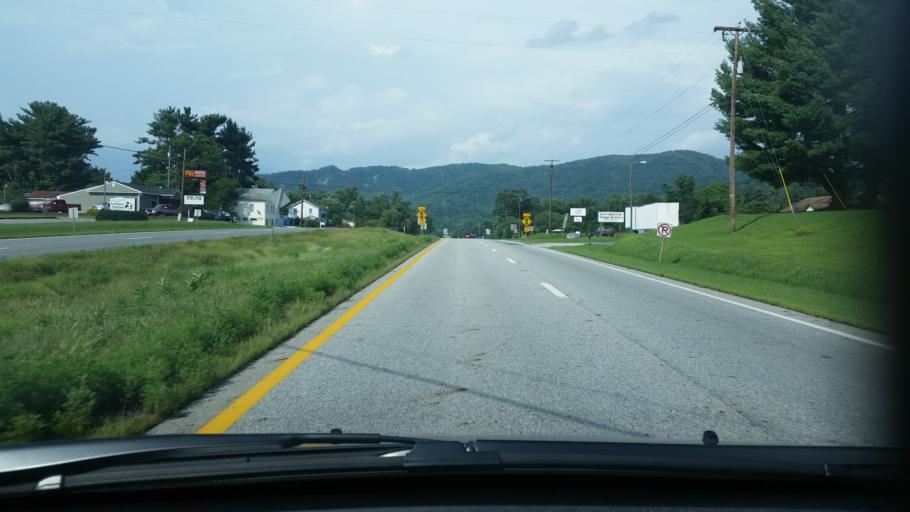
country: US
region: Virginia
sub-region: Nelson County
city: Lovingston
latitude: 37.7463
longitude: -78.8834
